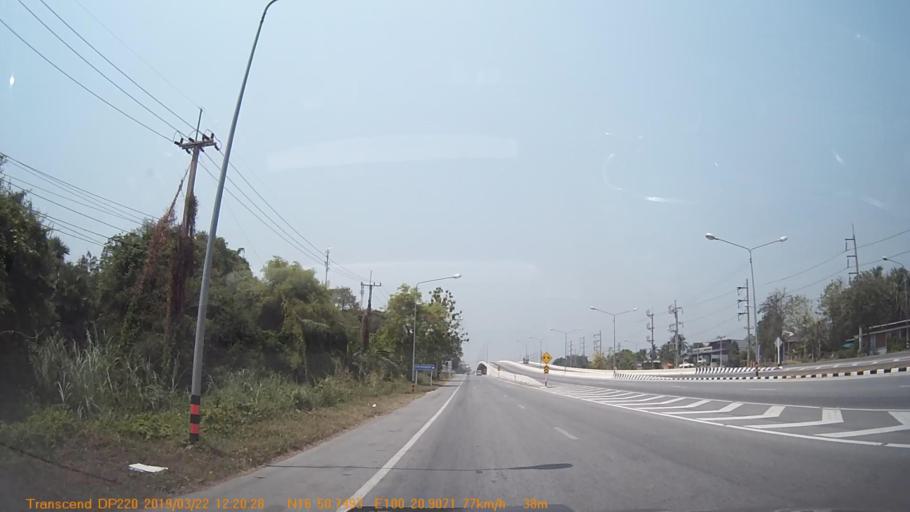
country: TH
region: Phitsanulok
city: Wang Thong
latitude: 16.8460
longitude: 100.3481
